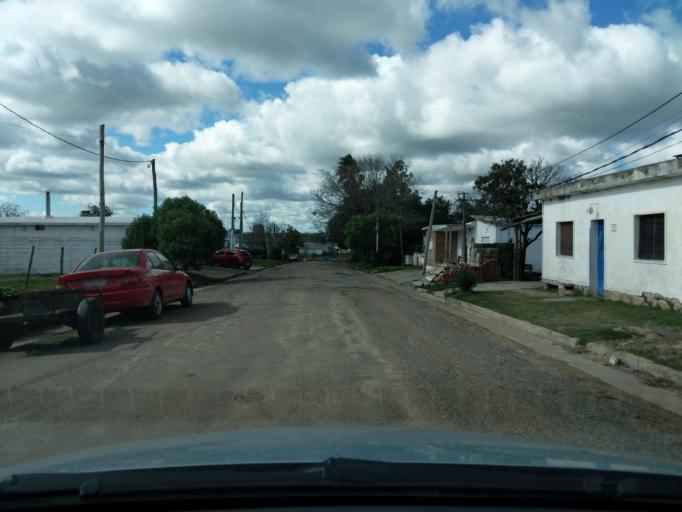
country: UY
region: Florida
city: Florida
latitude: -34.0945
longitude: -56.2299
